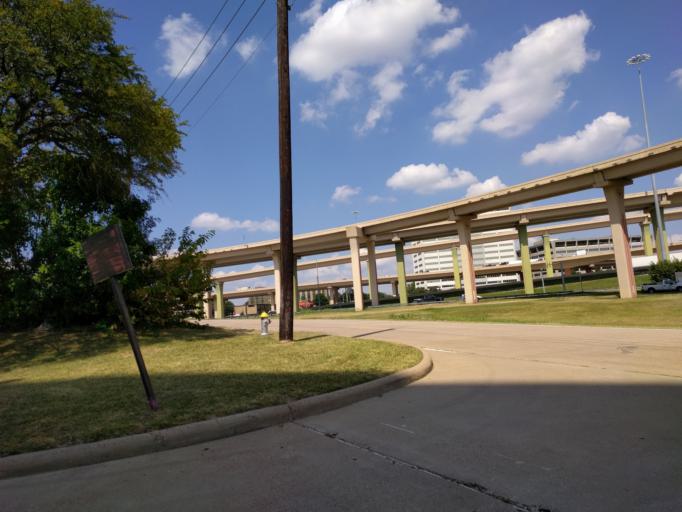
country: US
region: Texas
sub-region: Dallas County
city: Richardson
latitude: 32.9224
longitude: -96.7664
